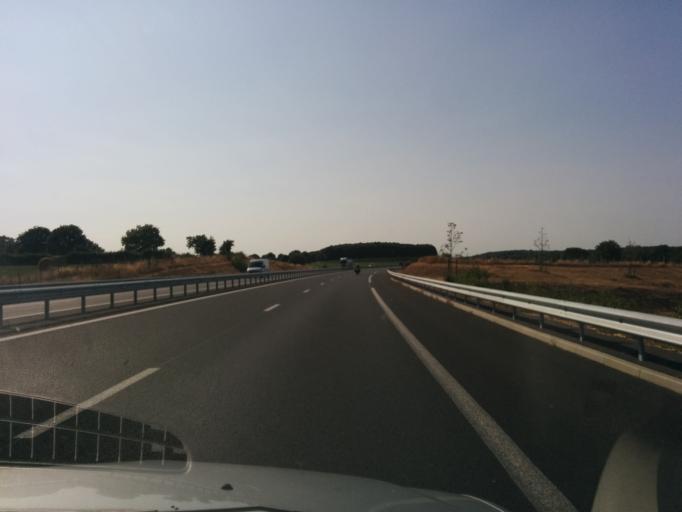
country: FR
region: Poitou-Charentes
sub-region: Departement des Deux-Sevres
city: Nueil-les-Aubiers
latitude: 46.8808
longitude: -0.5960
